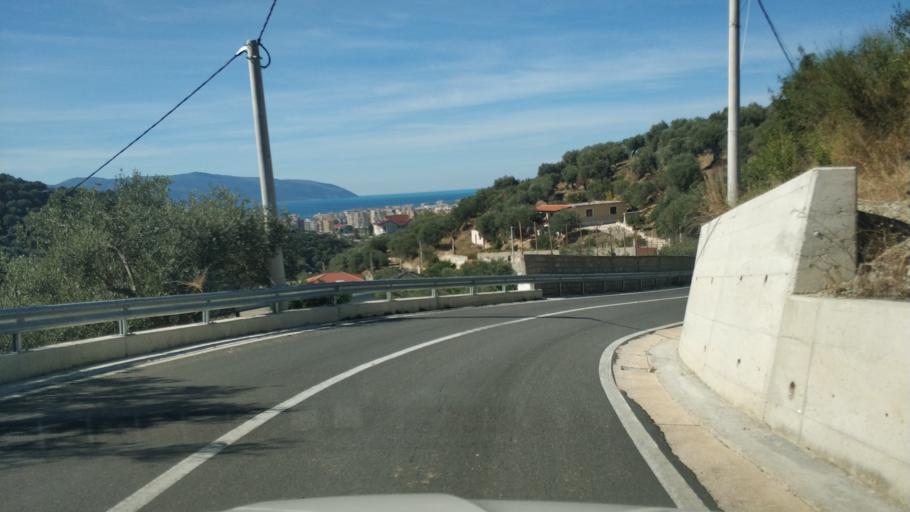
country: AL
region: Vlore
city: Vlore
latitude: 40.4572
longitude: 19.5058
